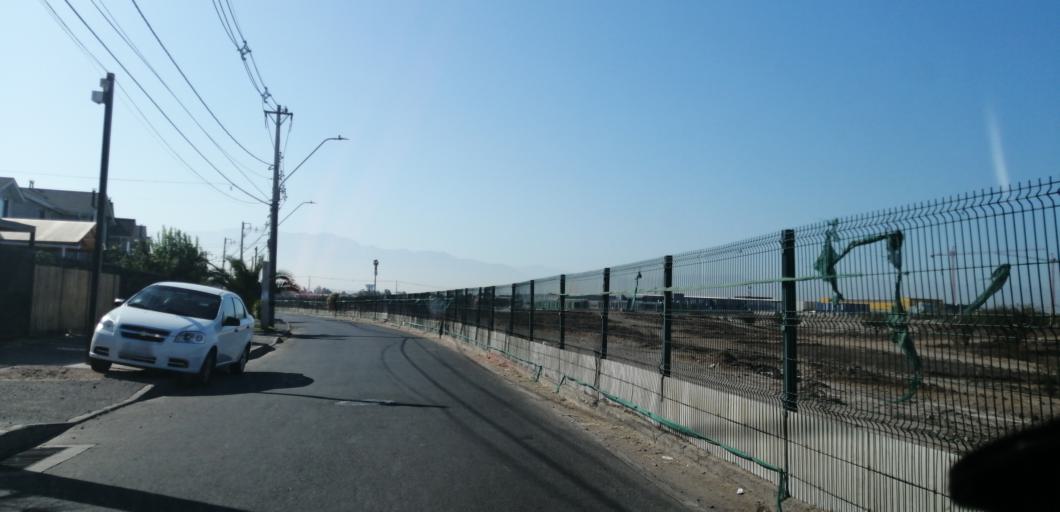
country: CL
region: Santiago Metropolitan
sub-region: Provincia de Santiago
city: Lo Prado
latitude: -33.4369
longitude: -70.7783
